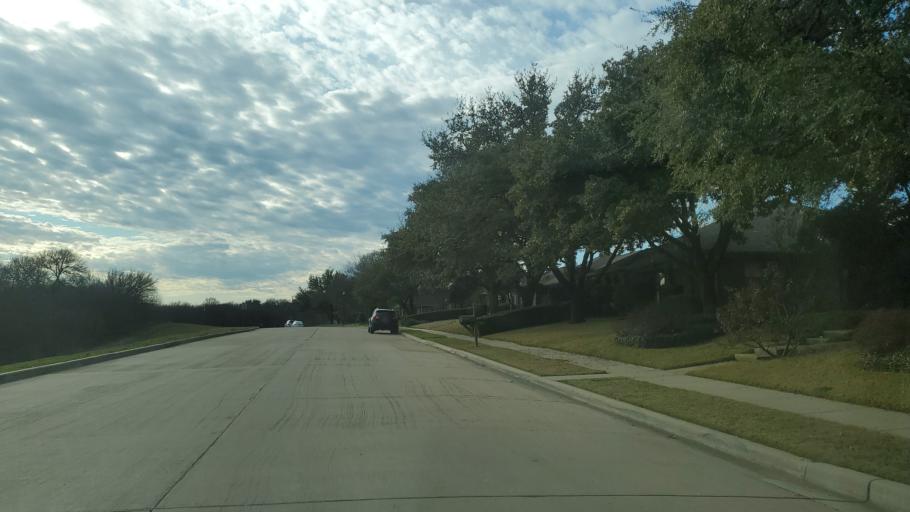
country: US
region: Texas
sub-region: Dallas County
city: Carrollton
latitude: 32.9929
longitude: -96.8994
